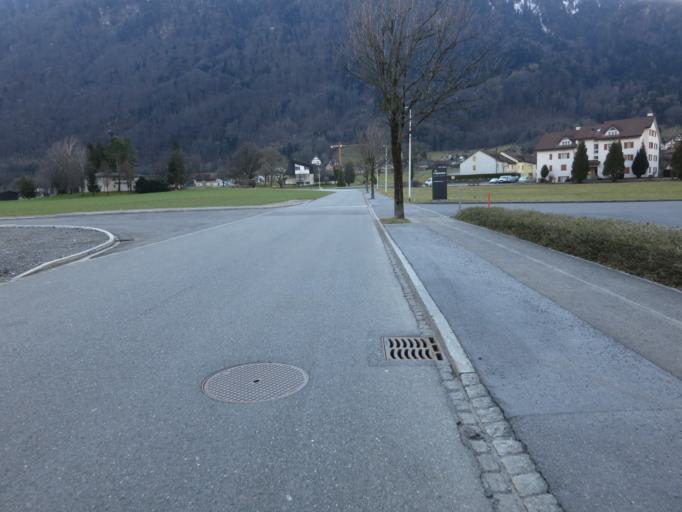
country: CH
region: Glarus
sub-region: Glarus
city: Bilten
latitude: 47.1507
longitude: 9.0285
